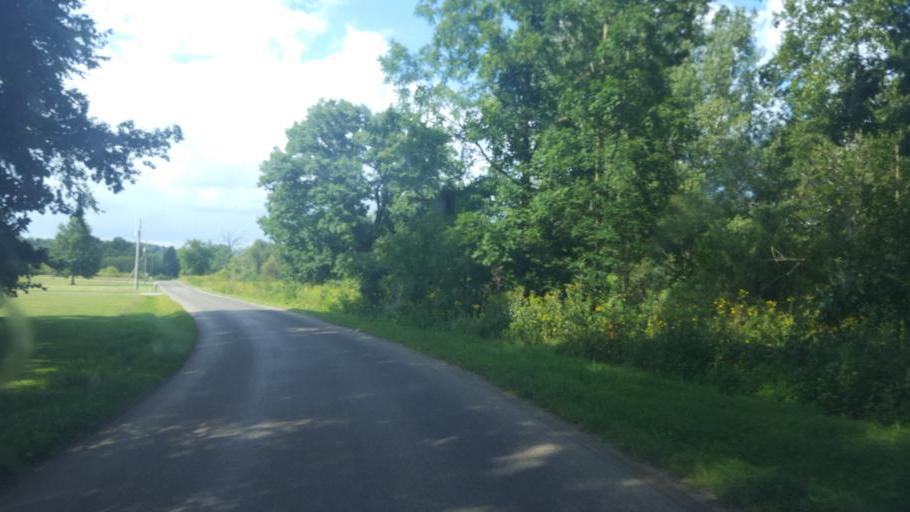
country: US
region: Ohio
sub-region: Knox County
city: Danville
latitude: 40.4593
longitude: -82.2869
